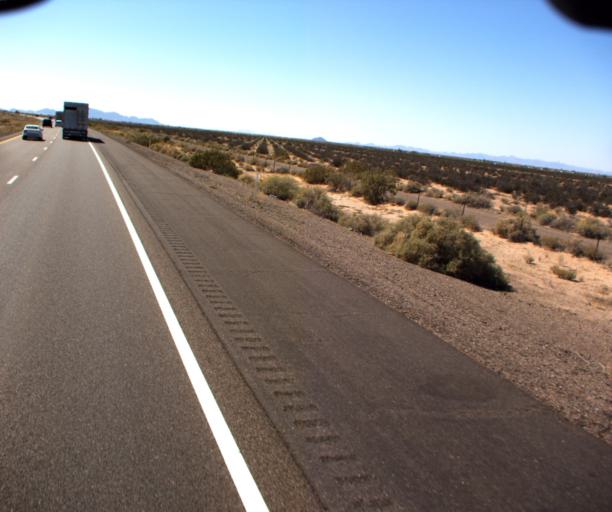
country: US
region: Arizona
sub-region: Yuma County
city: Wellton
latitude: 32.8176
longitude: -113.4958
